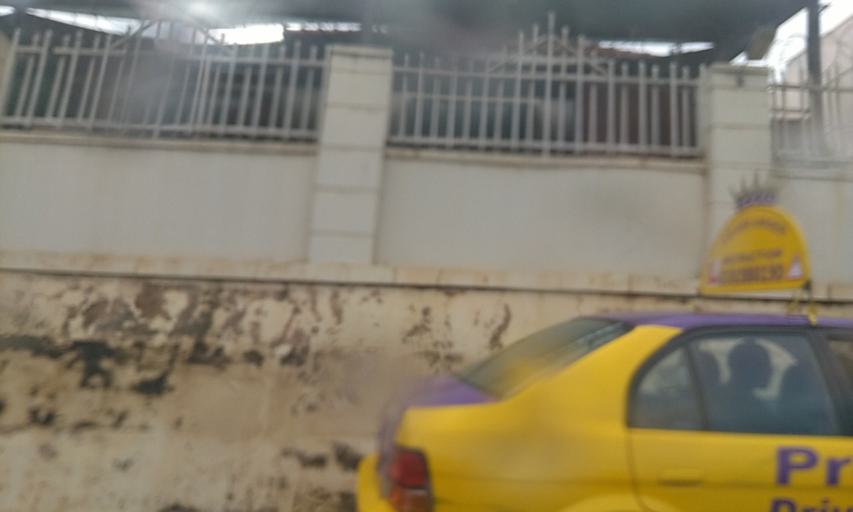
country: UG
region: Central Region
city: Kampala Central Division
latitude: 0.3426
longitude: 32.5901
